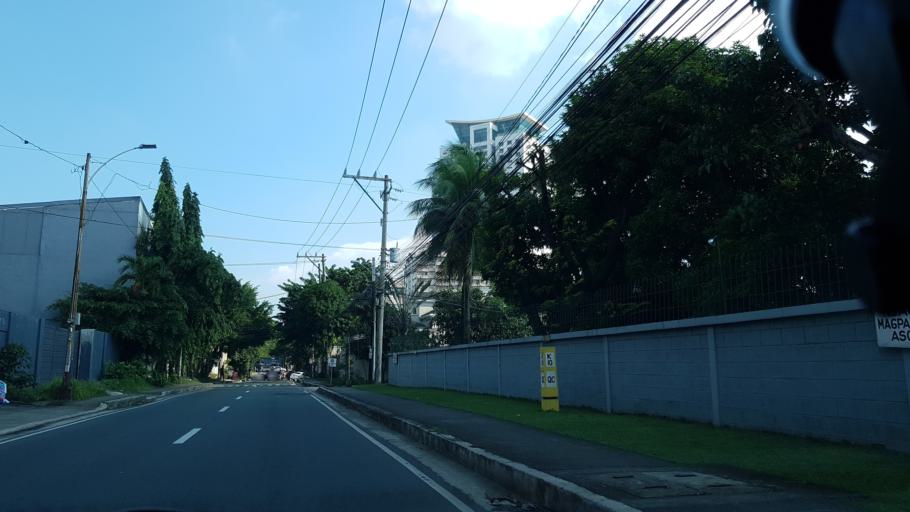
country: PH
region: Metro Manila
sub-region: San Juan
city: San Juan
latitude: 14.6187
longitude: 121.0385
